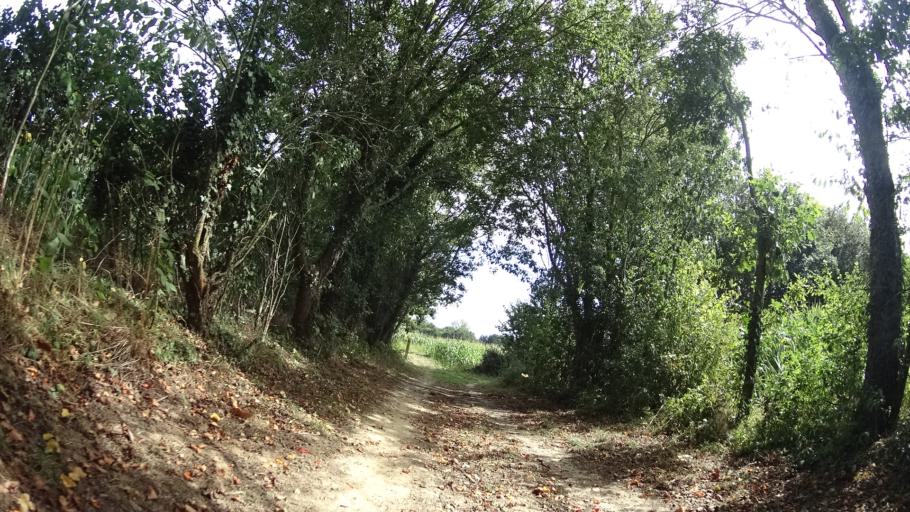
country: FR
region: Brittany
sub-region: Departement d'Ille-et-Vilaine
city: La Meziere
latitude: 48.2242
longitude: -1.7342
